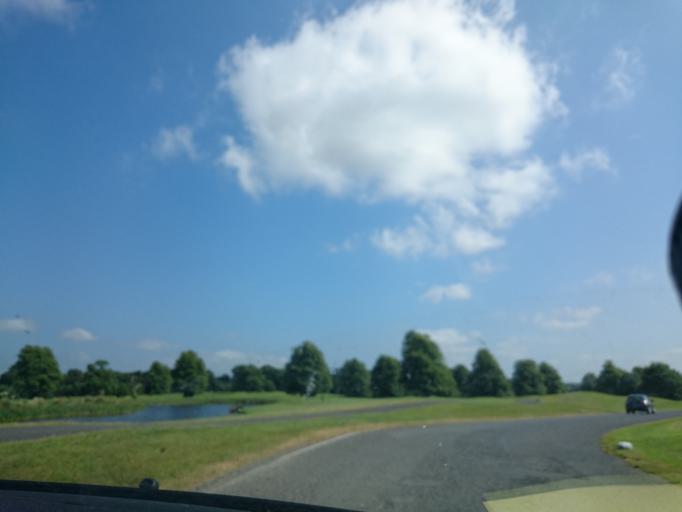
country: IE
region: Leinster
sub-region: Kilkenny
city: Thomastown
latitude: 52.5237
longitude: -7.1896
